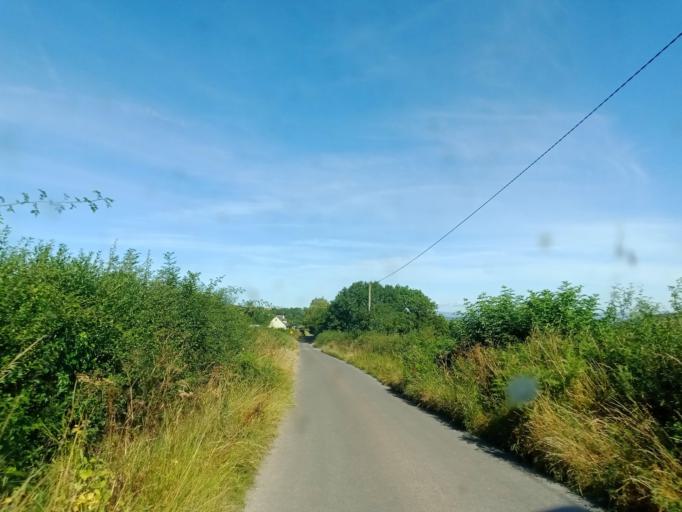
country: IE
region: Leinster
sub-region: Kilkenny
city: Ballyragget
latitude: 52.8000
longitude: -7.4271
